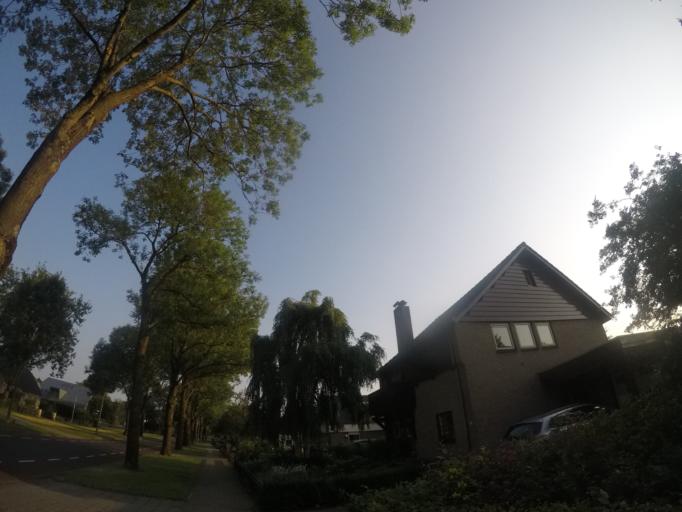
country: NL
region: Gelderland
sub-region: Gemeente Westervoort
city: Westervoort
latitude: 51.9536
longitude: 5.9717
